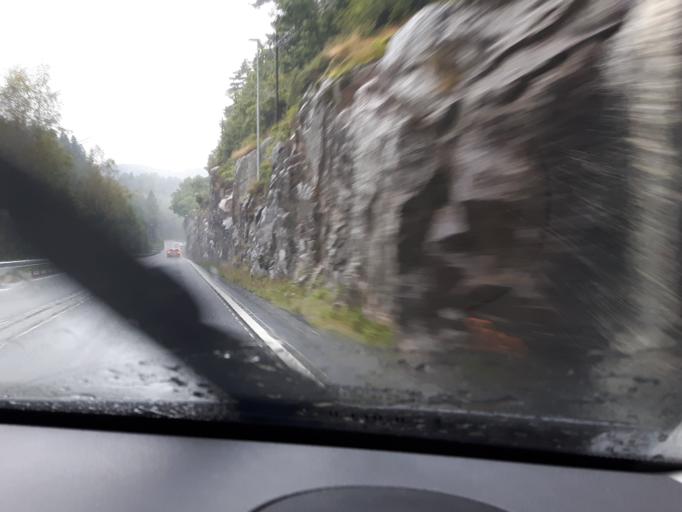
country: NO
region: Vest-Agder
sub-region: Mandal
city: Mandal
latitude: 58.0527
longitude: 7.3811
